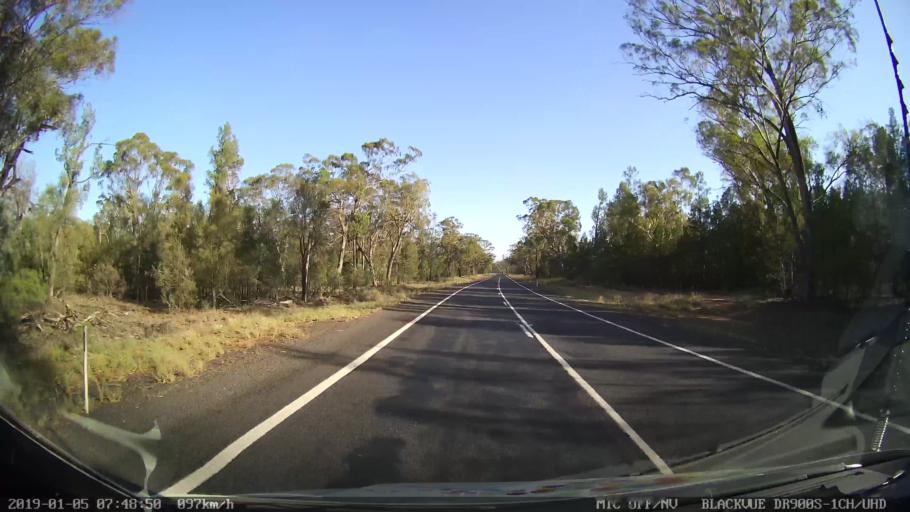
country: AU
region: New South Wales
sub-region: Gilgandra
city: Gilgandra
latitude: -31.8106
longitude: 148.6364
